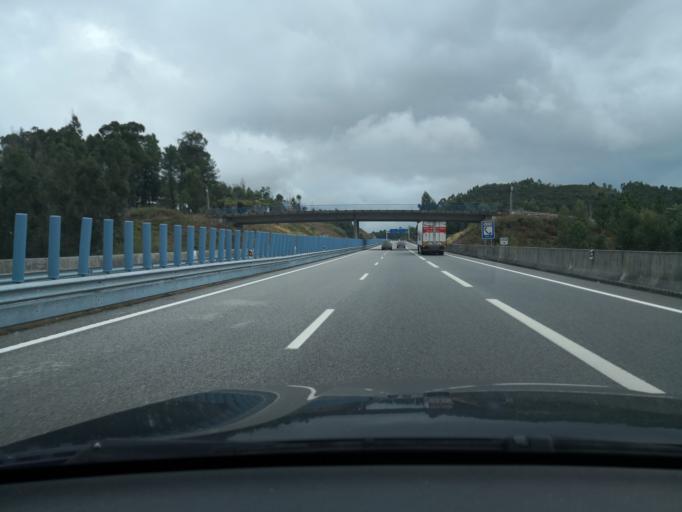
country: PT
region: Porto
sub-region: Lousada
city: Lousada
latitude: 41.2953
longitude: -8.2980
